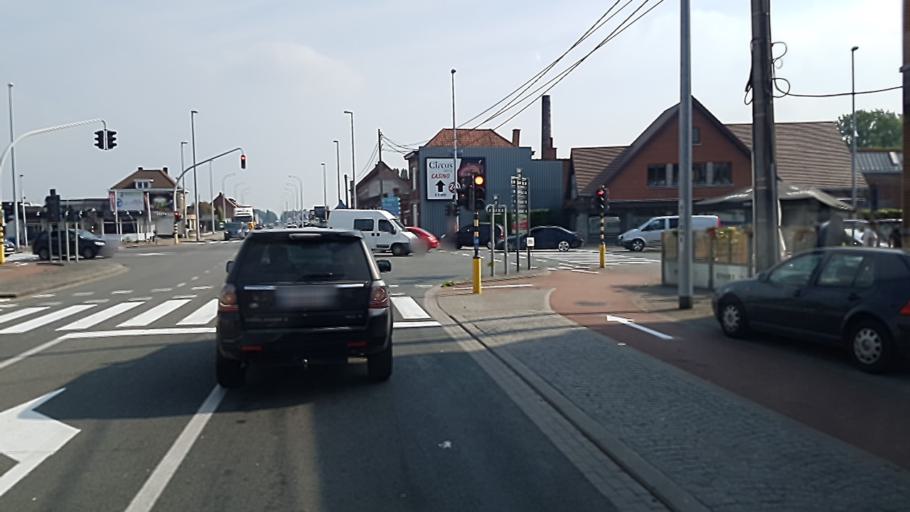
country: BE
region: Wallonia
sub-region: Province du Hainaut
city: Pecq
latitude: 50.7296
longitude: 3.3294
